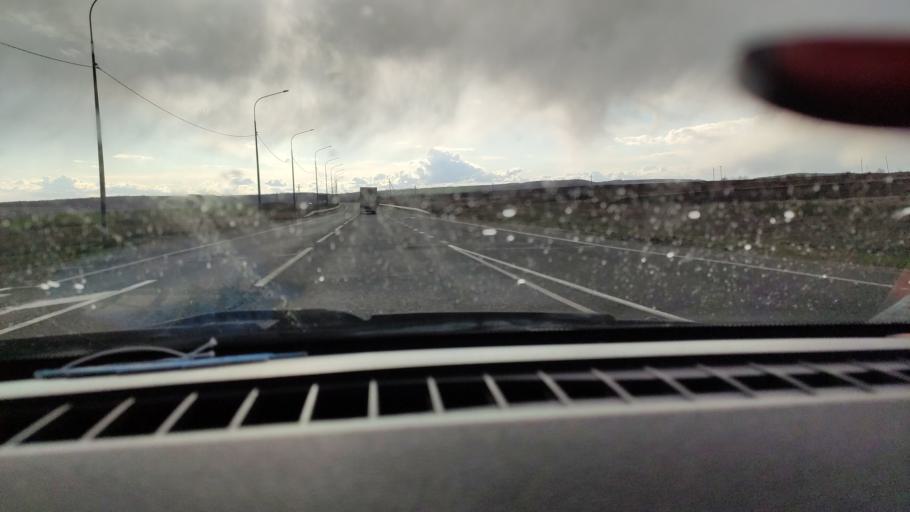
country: RU
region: Saratov
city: Yelshanka
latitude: 51.8299
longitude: 46.4098
